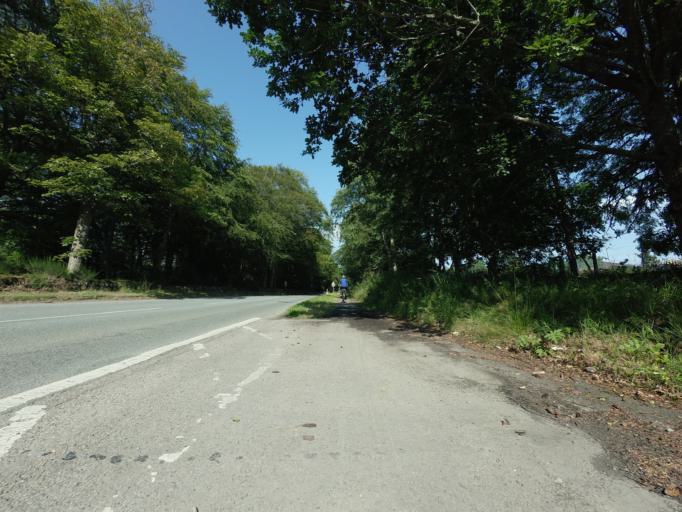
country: GB
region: Scotland
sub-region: Highland
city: Evanton
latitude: 57.6778
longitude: -4.3076
